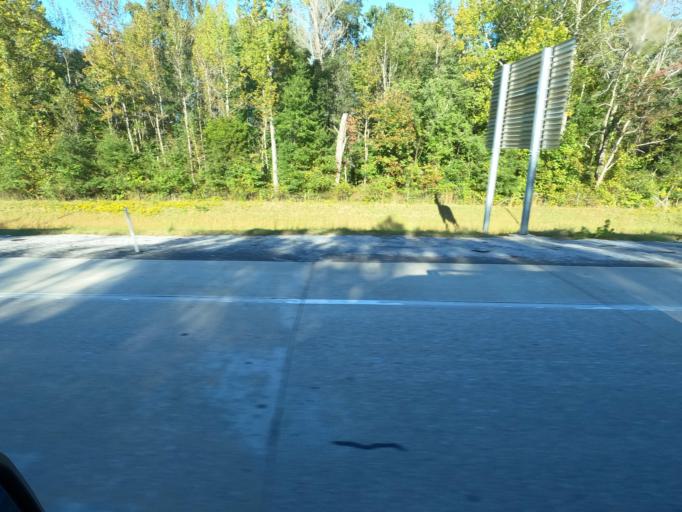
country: US
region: Tennessee
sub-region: Coffee County
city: Manchester
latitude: 35.4375
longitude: -86.0363
